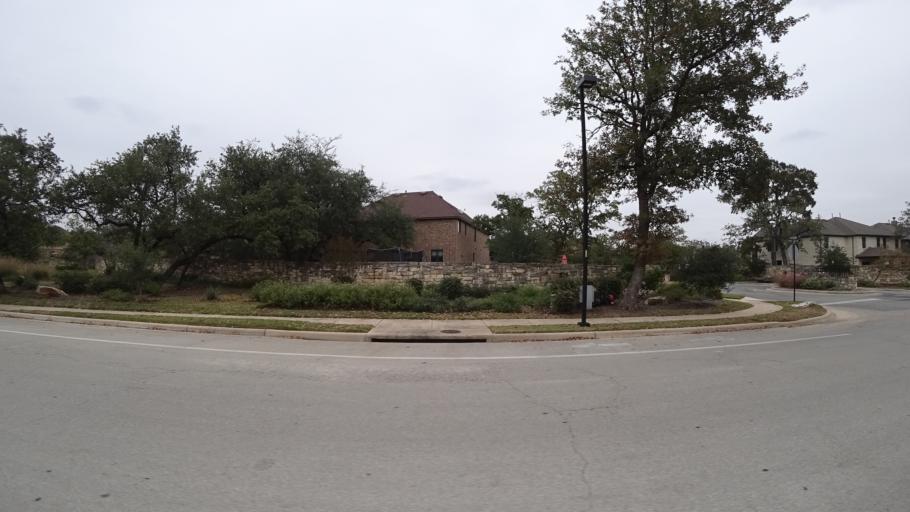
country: US
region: Texas
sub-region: Travis County
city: Shady Hollow
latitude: 30.1941
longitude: -97.9116
